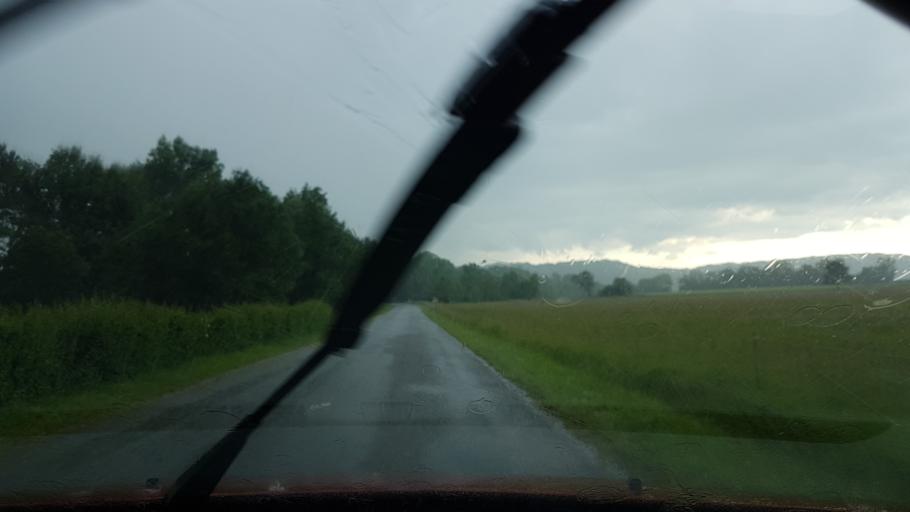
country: FR
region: Franche-Comte
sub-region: Departement du Jura
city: Clairvaux-les-Lacs
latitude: 46.5534
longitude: 5.7171
